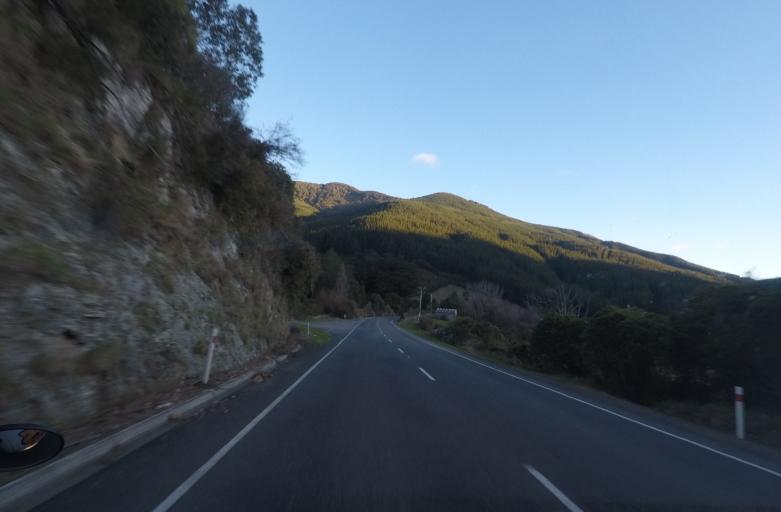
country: NZ
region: Marlborough
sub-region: Marlborough District
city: Picton
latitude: -41.2800
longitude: 173.7277
